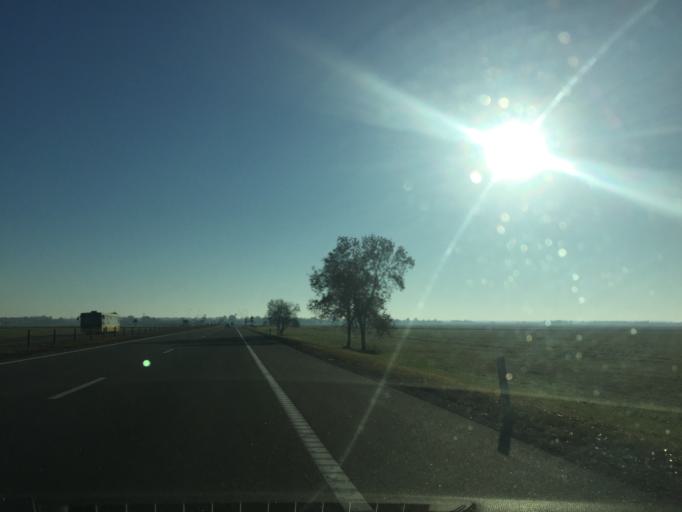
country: BY
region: Minsk
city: Smilavichy
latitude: 53.7598
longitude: 27.9517
